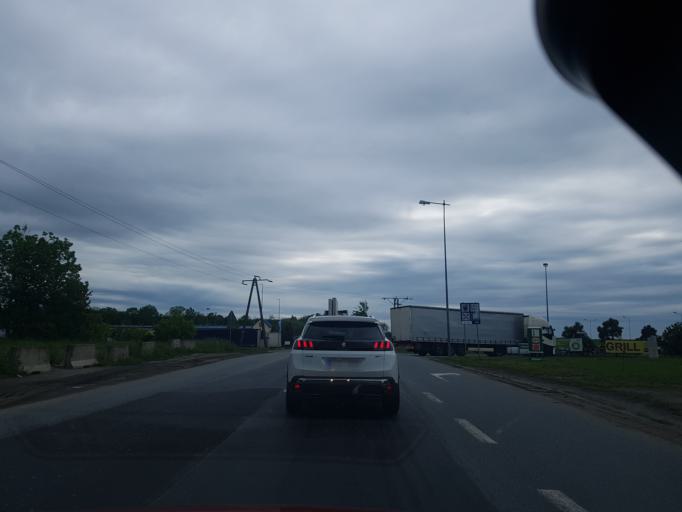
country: PL
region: Lower Silesian Voivodeship
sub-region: Powiat wroclawski
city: Katy Wroclawskie
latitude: 51.0194
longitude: 16.7547
